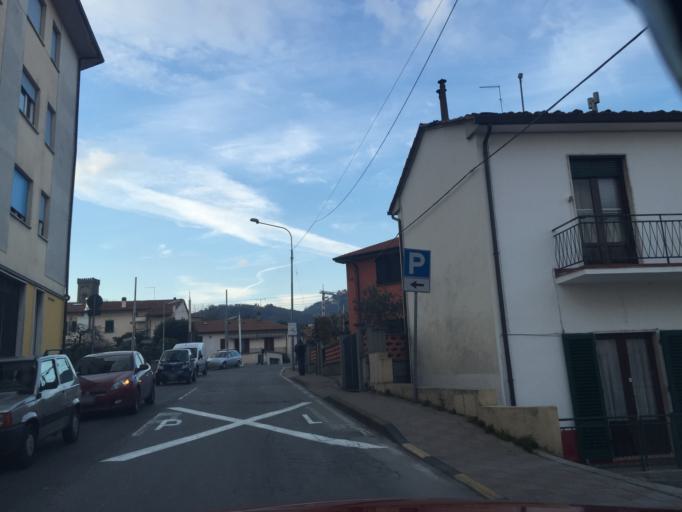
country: IT
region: Tuscany
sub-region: Provincia di Pistoia
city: Pieve a Nievole
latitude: 43.8782
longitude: 10.7968
